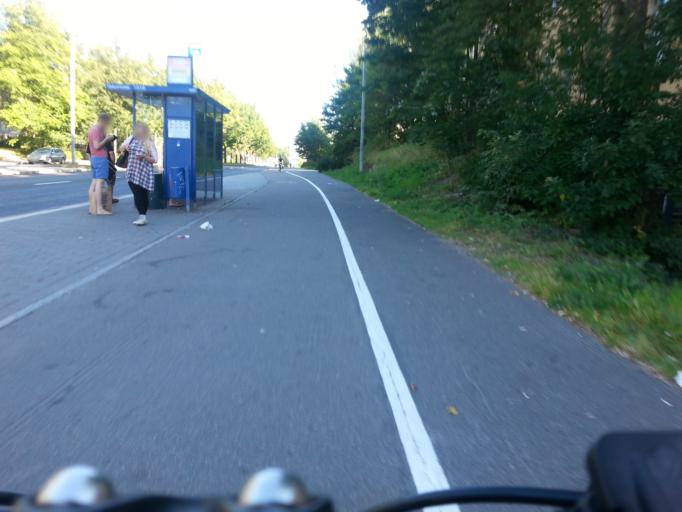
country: FI
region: Uusimaa
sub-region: Helsinki
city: Teekkarikylae
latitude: 60.2170
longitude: 24.8701
